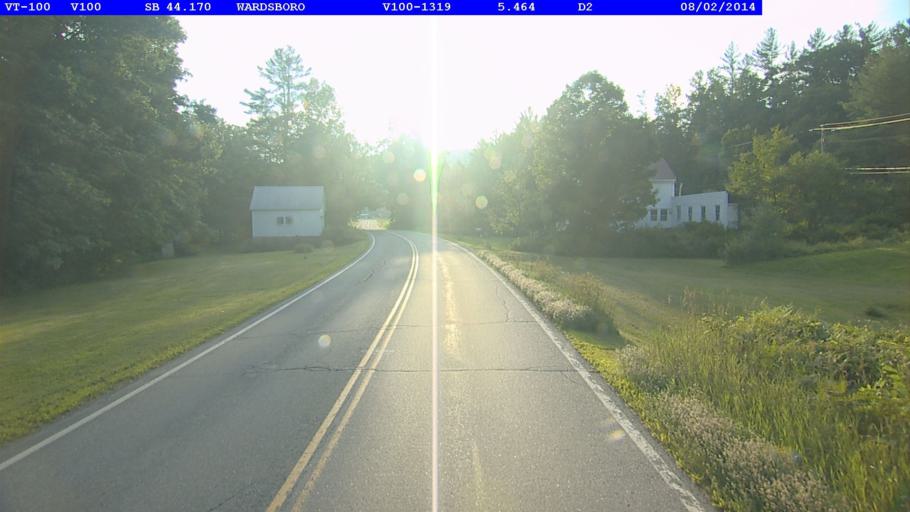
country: US
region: Vermont
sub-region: Windham County
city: Dover
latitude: 43.0344
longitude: -72.8051
